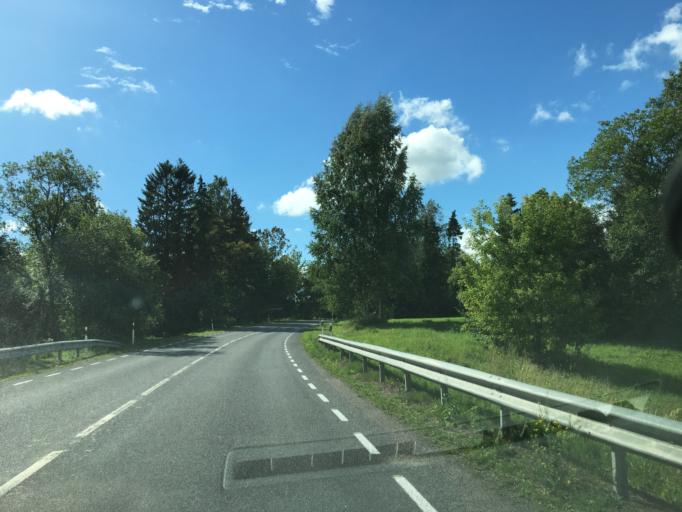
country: EE
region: Paernumaa
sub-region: Vaendra vald (alev)
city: Vandra
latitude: 58.5745
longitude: 25.2000
